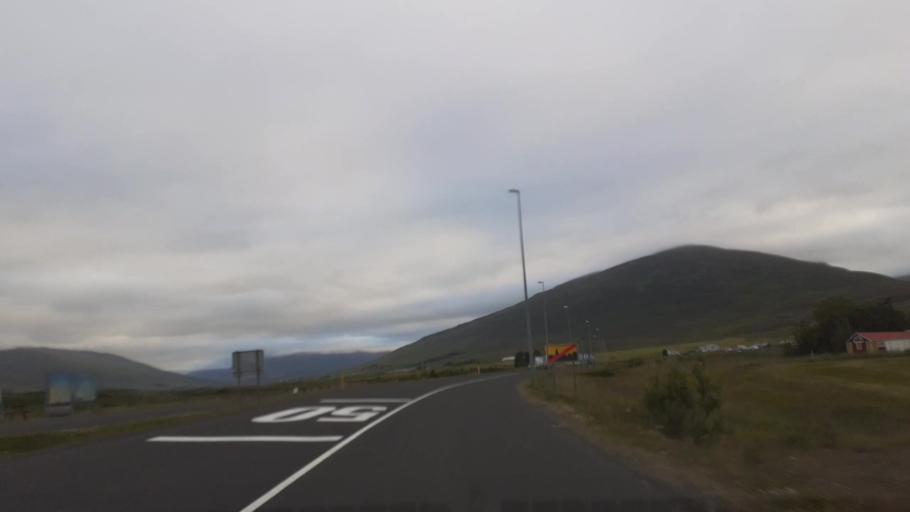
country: IS
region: Northeast
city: Dalvik
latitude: 65.9639
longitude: -18.5342
